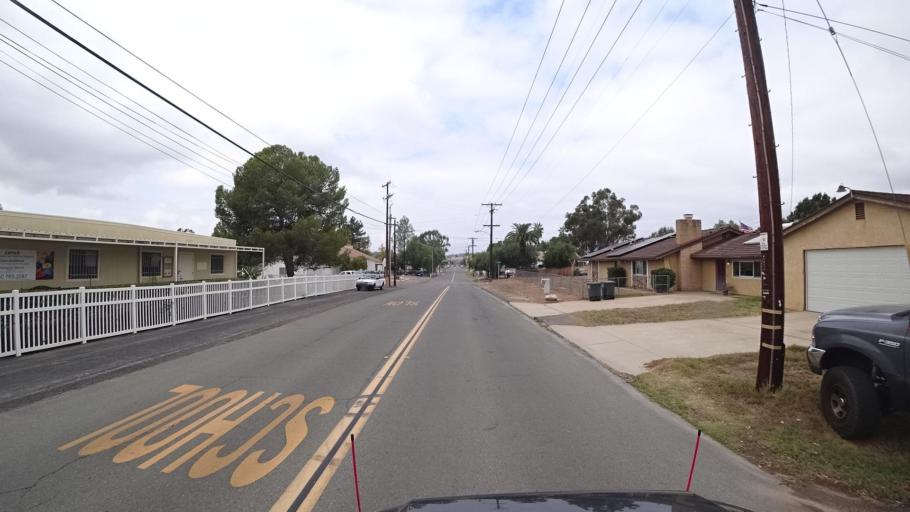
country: US
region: California
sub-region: San Diego County
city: Ramona
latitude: 33.0407
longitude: -116.8630
